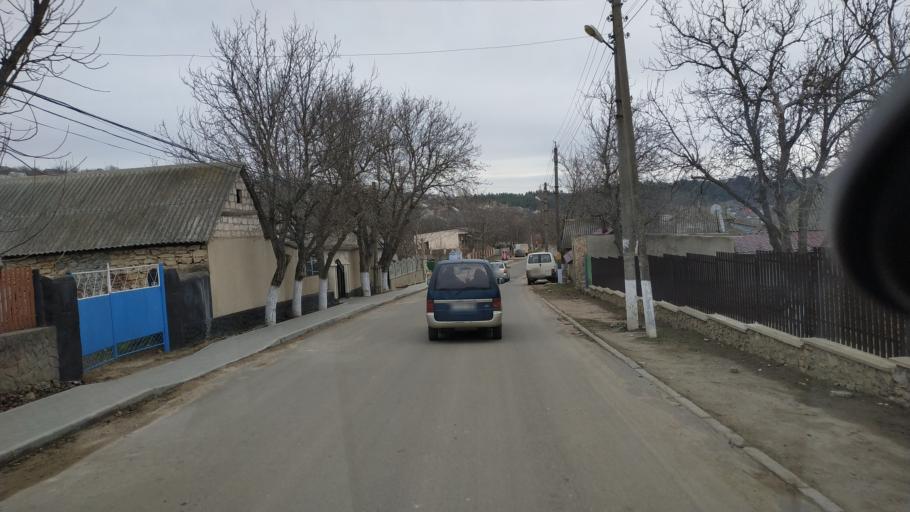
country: MD
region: Telenesti
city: Cocieri
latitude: 47.2695
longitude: 29.0619
